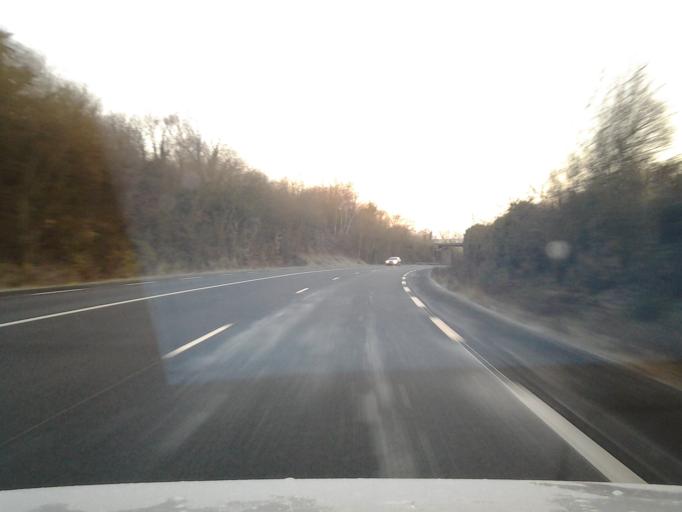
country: FR
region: Pays de la Loire
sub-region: Departement de la Vendee
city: Chambretaud
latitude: 46.9173
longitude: -0.9692
